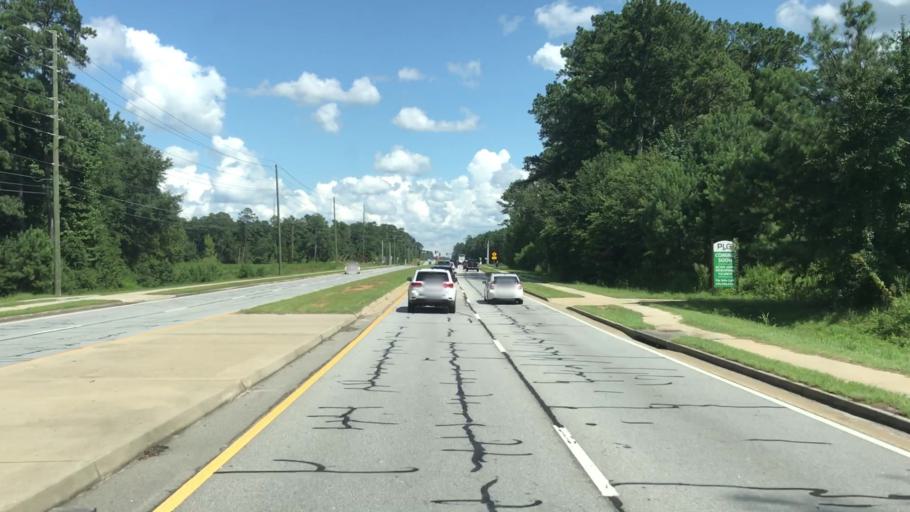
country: US
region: Georgia
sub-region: Gwinnett County
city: Grayson
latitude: 33.8797
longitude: -83.9355
